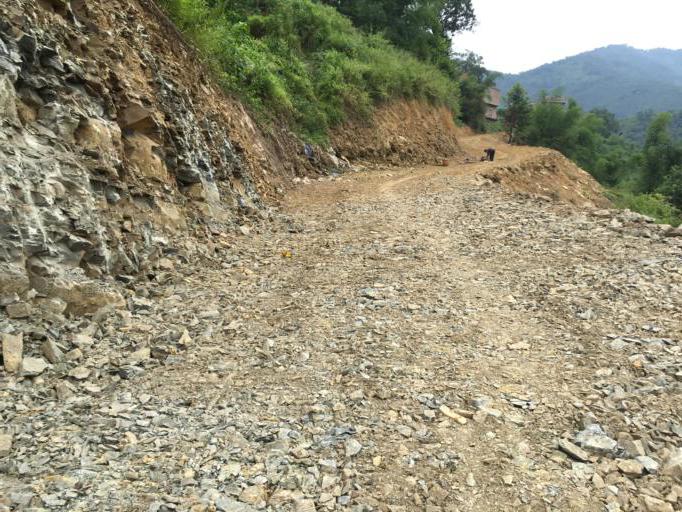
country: CN
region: Guangxi Zhuangzu Zizhiqu
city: Tongle
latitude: 25.1218
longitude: 106.4233
